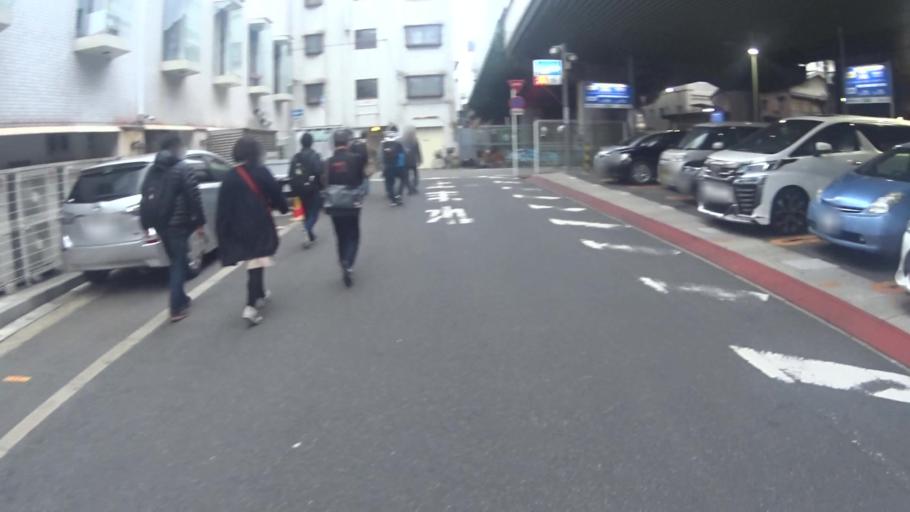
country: JP
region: Osaka
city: Osaka-shi
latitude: 34.6662
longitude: 135.5107
